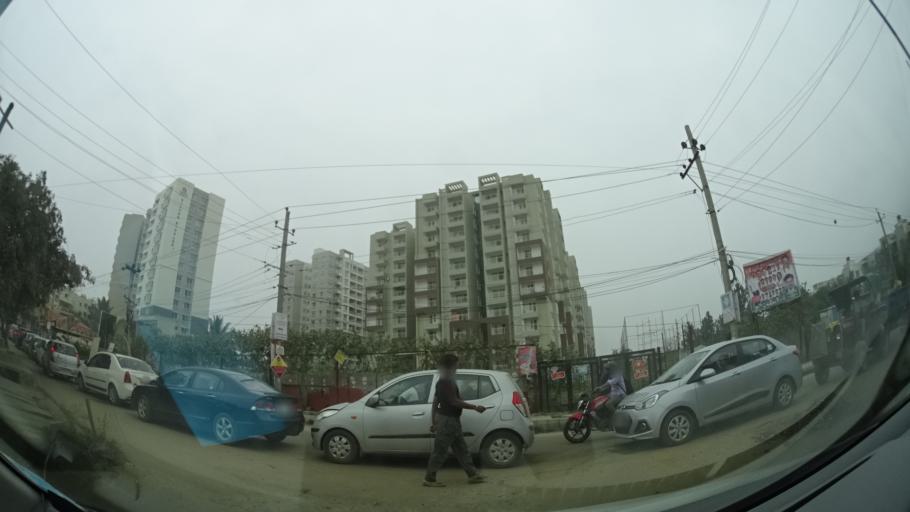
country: IN
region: Karnataka
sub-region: Bangalore Rural
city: Hoskote
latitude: 12.9690
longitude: 77.7397
